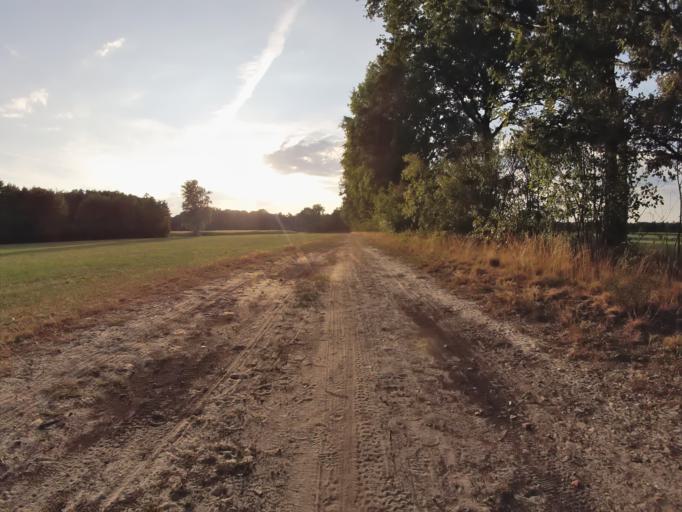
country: DE
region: North Rhine-Westphalia
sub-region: Regierungsbezirk Munster
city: Westerkappeln
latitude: 52.3701
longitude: 7.8858
